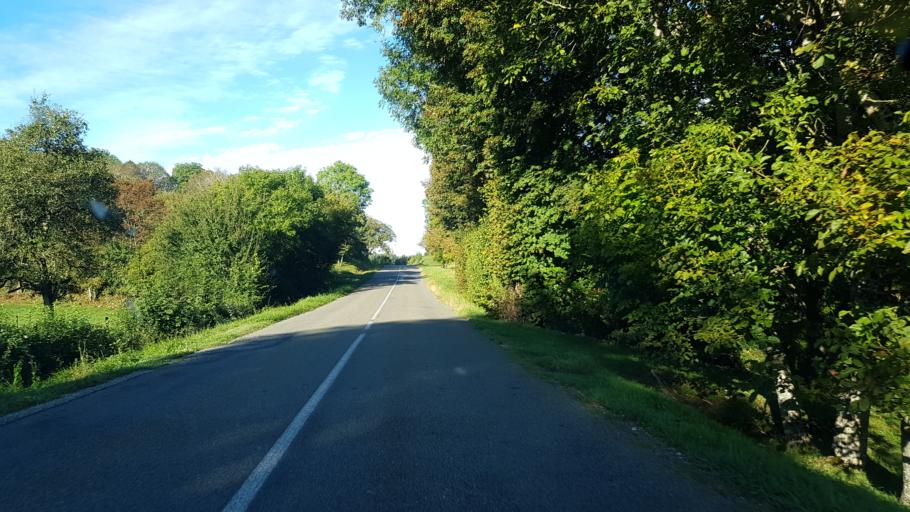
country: FR
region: Franche-Comte
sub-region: Departement du Jura
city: Cousance
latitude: 46.5516
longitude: 5.4906
